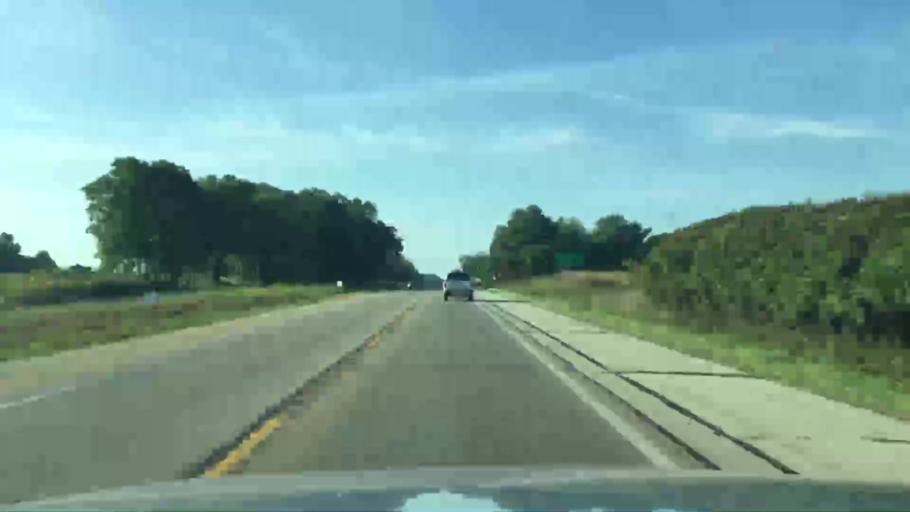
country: US
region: Michigan
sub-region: Jackson County
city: Vandercook Lake
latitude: 42.1055
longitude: -84.3640
